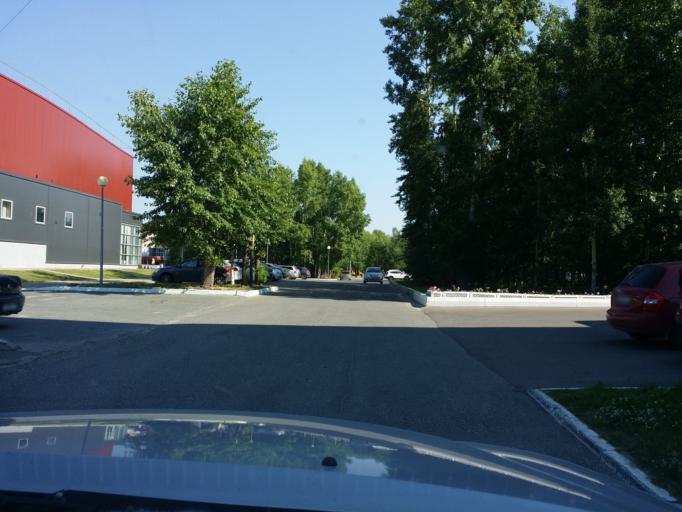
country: RU
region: Tomsk
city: Strezhevoy
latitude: 60.7252
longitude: 77.6044
